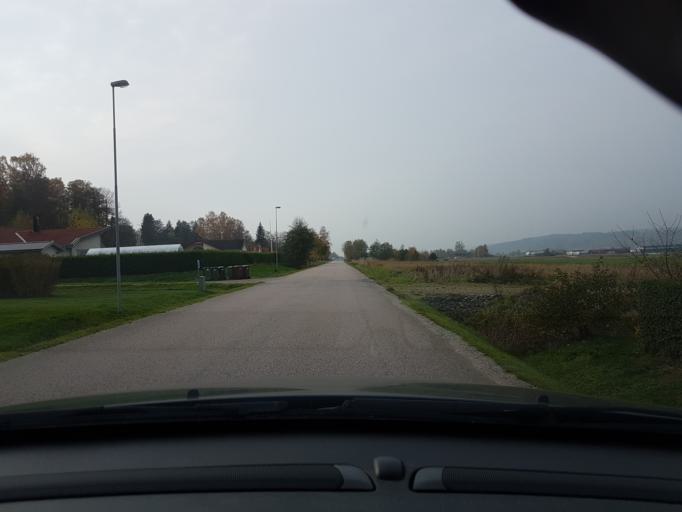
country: SE
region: Vaestra Goetaland
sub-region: Ale Kommun
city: Alvangen
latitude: 57.9682
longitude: 12.1591
